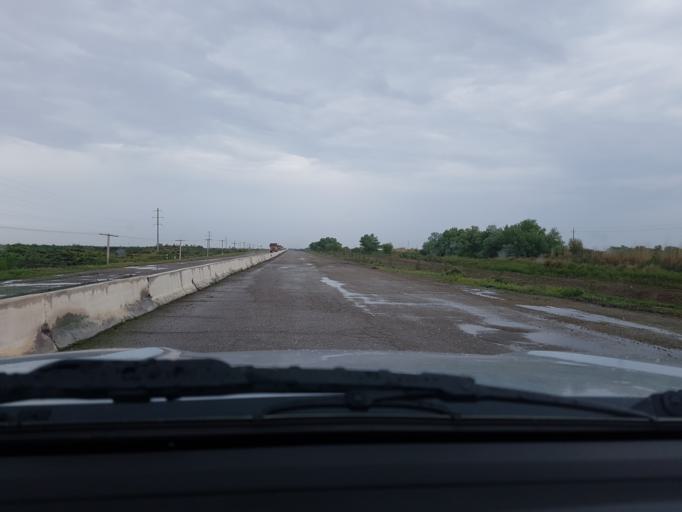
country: UZ
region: Bukhara
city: Olot
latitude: 39.2743
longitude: 63.7362
